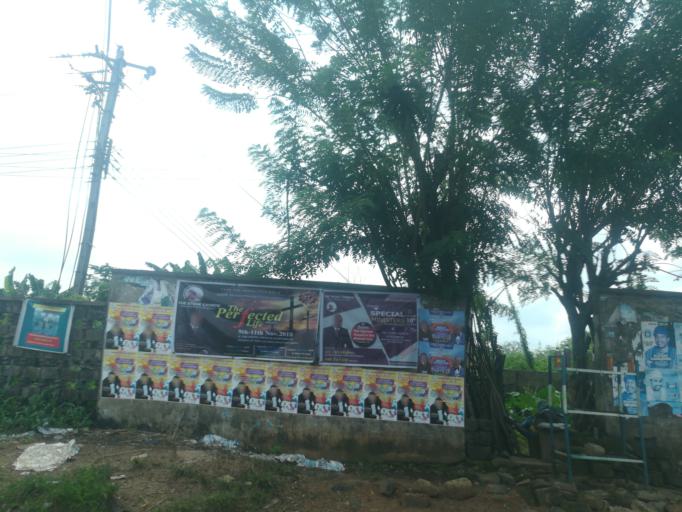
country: NG
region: Oyo
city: Ibadan
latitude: 7.3832
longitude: 3.8310
